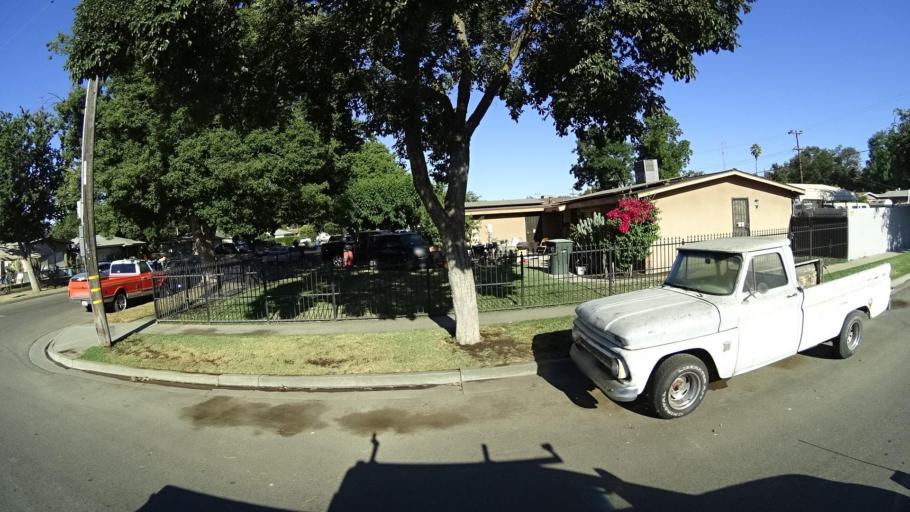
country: US
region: California
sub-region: Fresno County
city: Fresno
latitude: 36.7051
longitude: -119.7953
